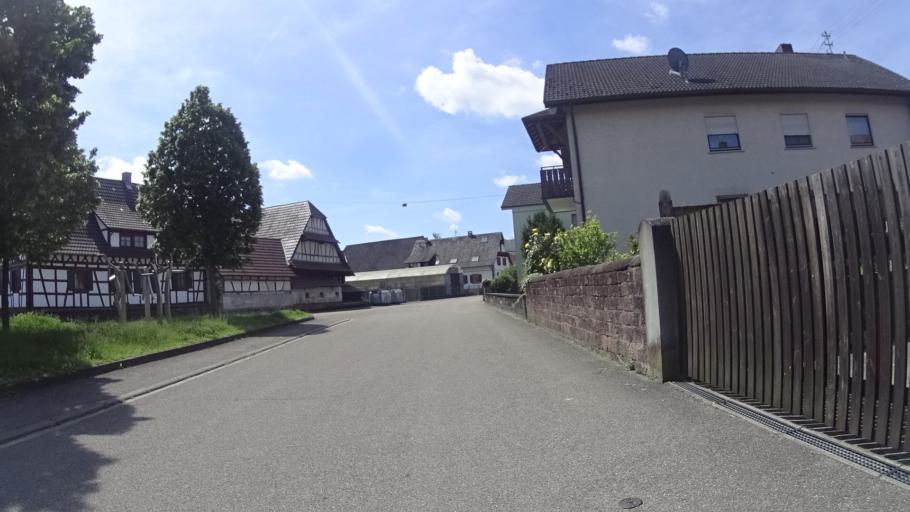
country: DE
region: Baden-Wuerttemberg
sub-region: Freiburg Region
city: Meissenheim
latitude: 48.4353
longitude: 7.8058
